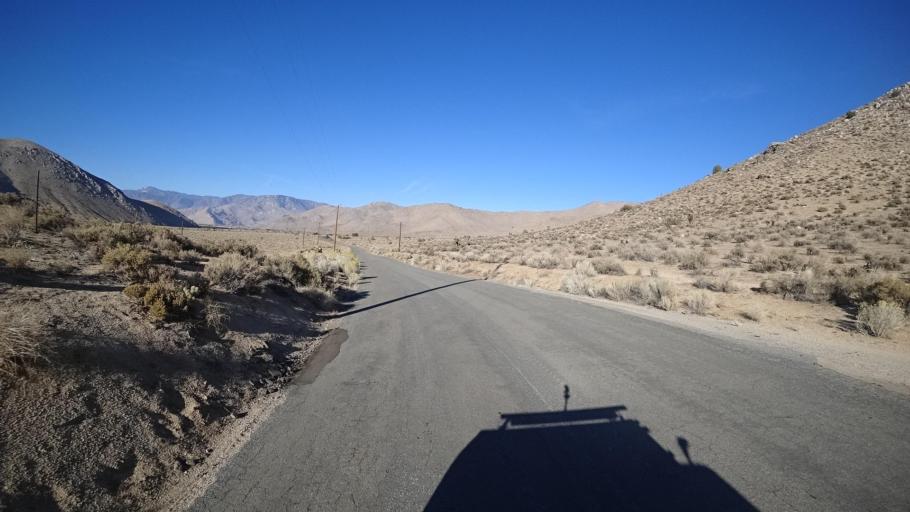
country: US
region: California
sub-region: Kern County
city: Weldon
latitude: 35.5906
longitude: -118.2404
